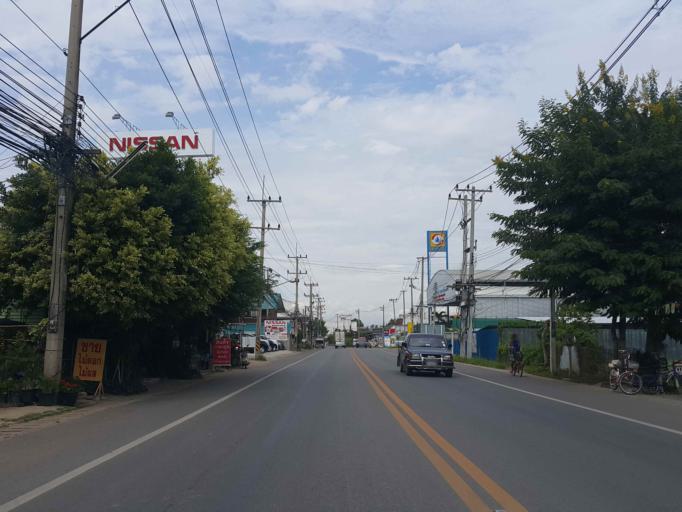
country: TH
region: Lamphun
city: Lamphun
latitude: 18.6030
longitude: 99.0218
